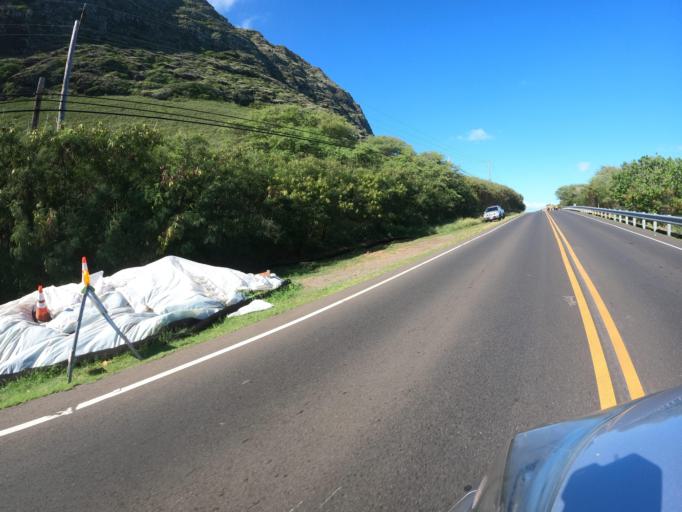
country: US
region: Hawaii
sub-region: Honolulu County
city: Waimanalo Beach
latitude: 21.3200
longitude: -157.6722
